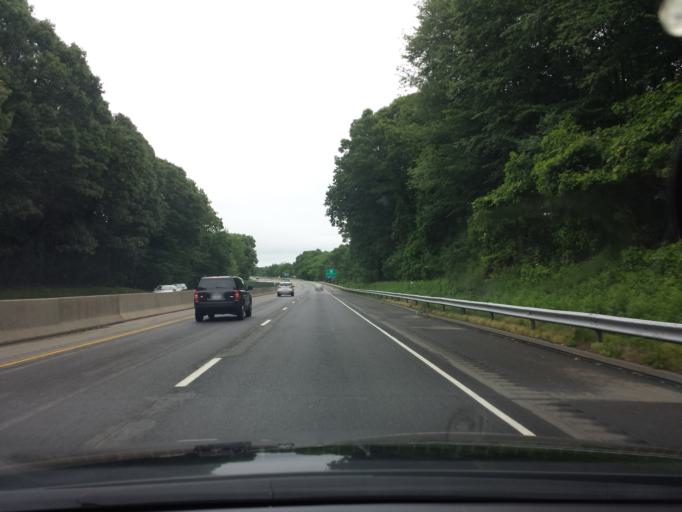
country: US
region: Connecticut
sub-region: Middlesex County
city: Saybrook Manor
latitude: 41.2961
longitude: -72.3992
